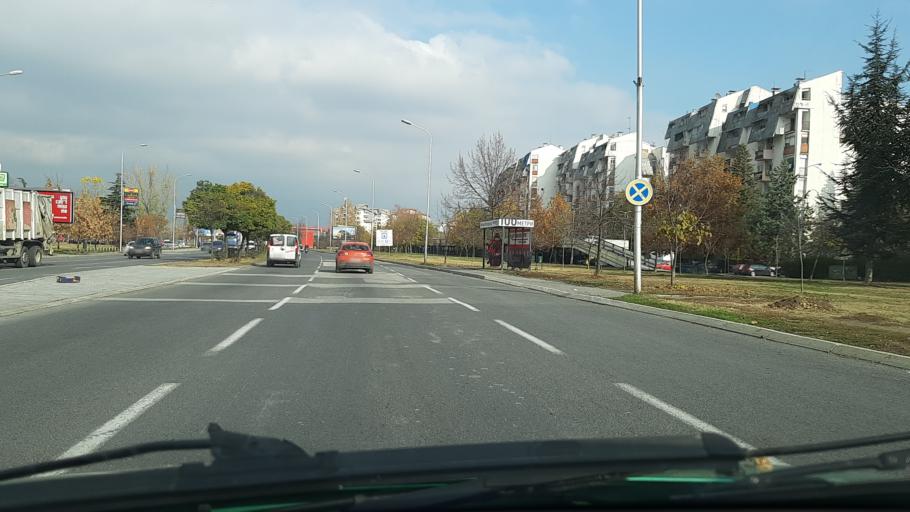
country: MK
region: Kisela Voda
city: Usje
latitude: 41.9831
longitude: 21.4716
